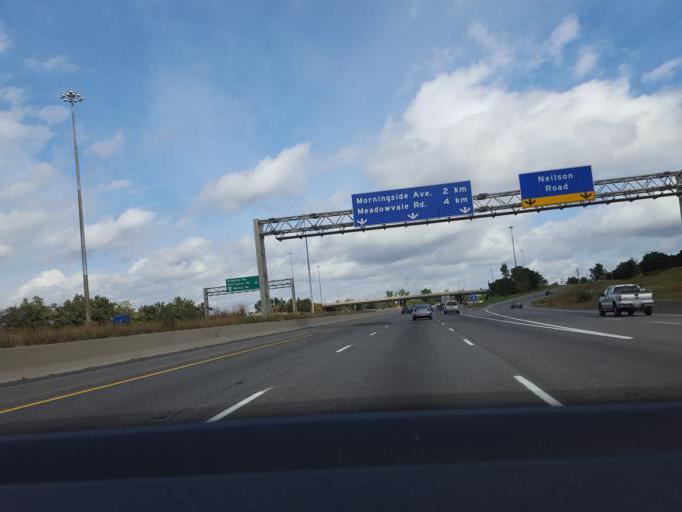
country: CA
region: Ontario
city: Scarborough
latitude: 43.7915
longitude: -79.2206
